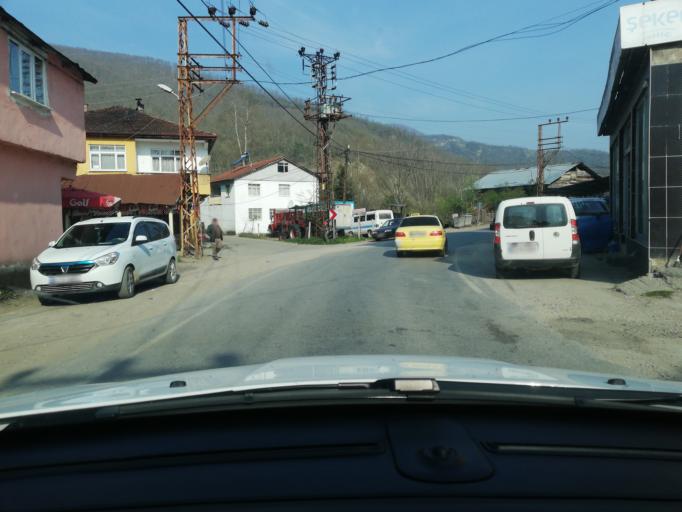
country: TR
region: Karabuk
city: Yenice
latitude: 41.2133
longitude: 32.3626
